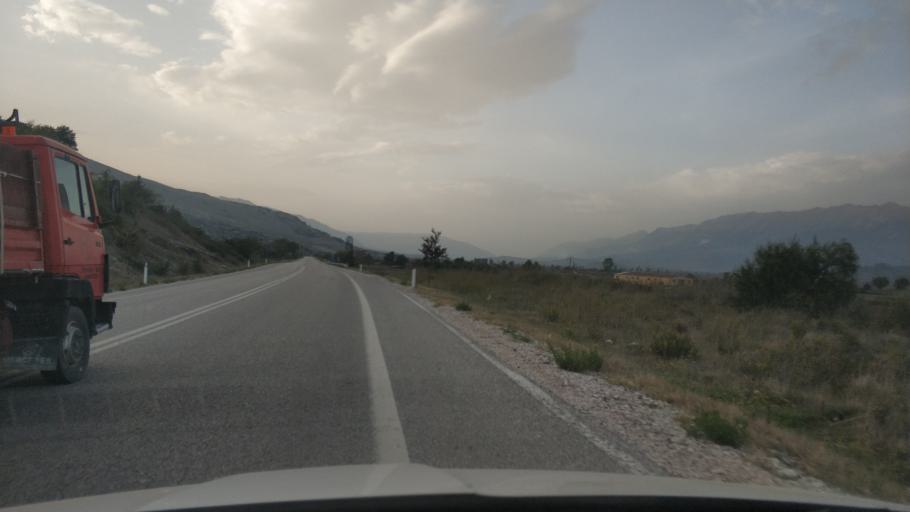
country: AL
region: Gjirokaster
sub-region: Rrethi i Gjirokastres
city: Libohove
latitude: 39.9497
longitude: 20.2570
